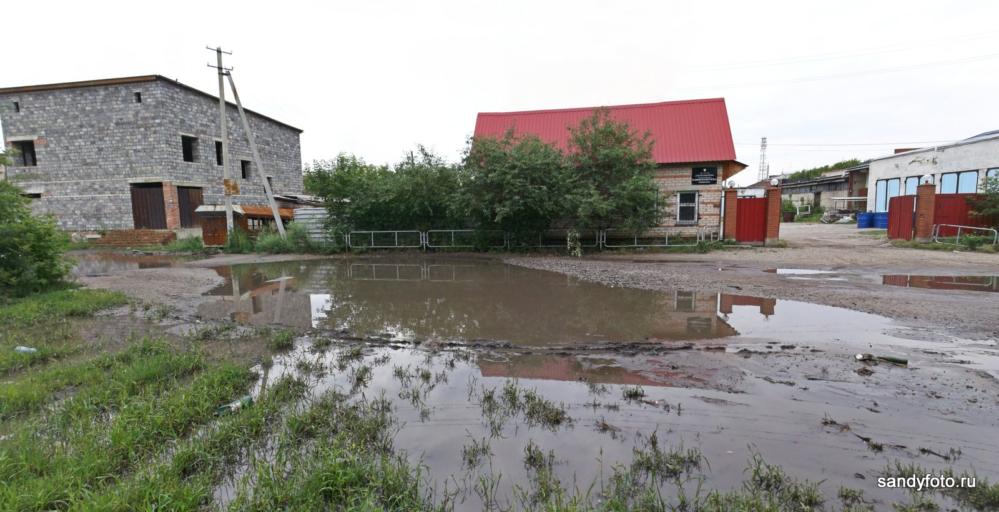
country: RU
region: Chelyabinsk
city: Troitsk
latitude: 54.0909
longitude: 61.5577
